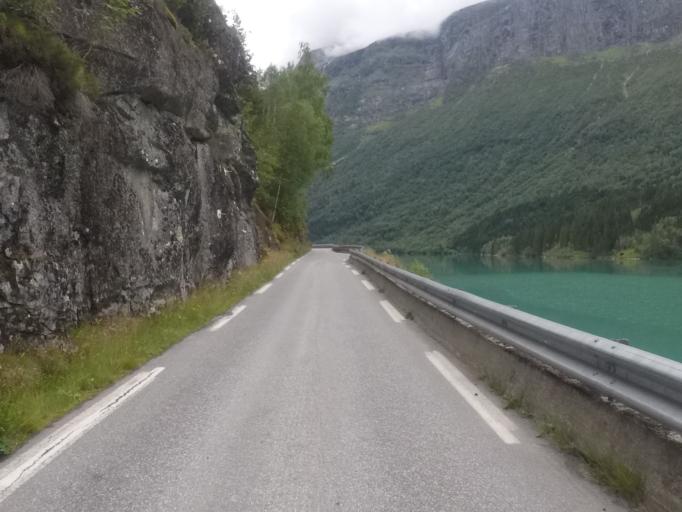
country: NO
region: Sogn og Fjordane
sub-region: Stryn
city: Stryn
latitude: 61.8565
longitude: 6.8955
